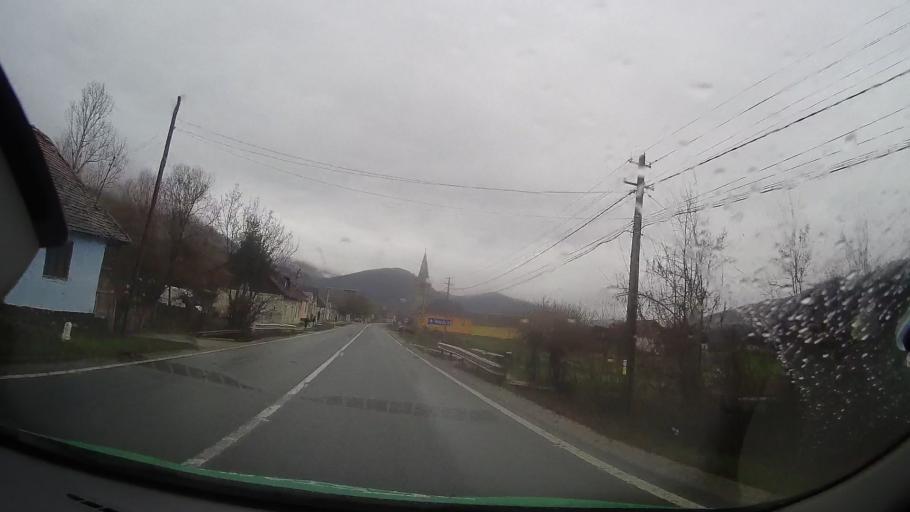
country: RO
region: Bistrita-Nasaud
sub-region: Comuna Teaca
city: Teaca
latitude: 46.9467
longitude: 24.4570
